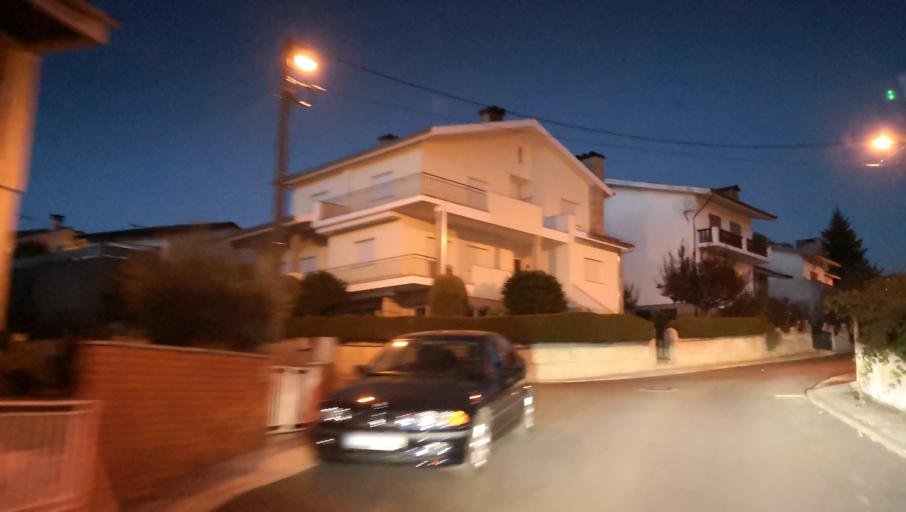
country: PT
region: Vila Real
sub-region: Vila Real
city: Vila Real
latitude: 41.2961
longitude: -7.7521
